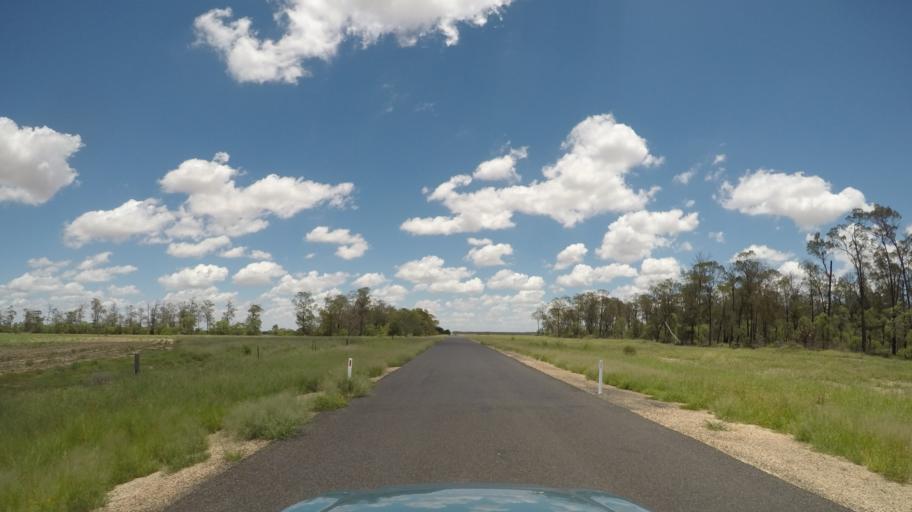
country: AU
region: Queensland
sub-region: Goondiwindi
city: Goondiwindi
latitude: -28.1725
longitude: 150.2312
